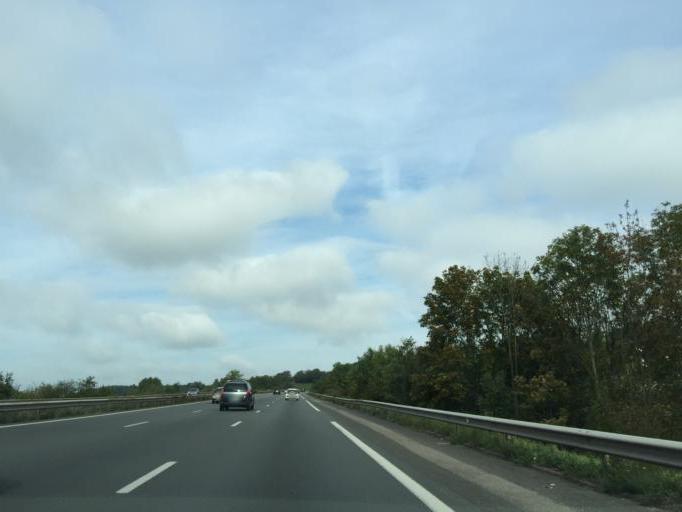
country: FR
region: Rhone-Alpes
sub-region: Departement de la Loire
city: La Fouillouse
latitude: 45.5032
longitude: 4.3074
